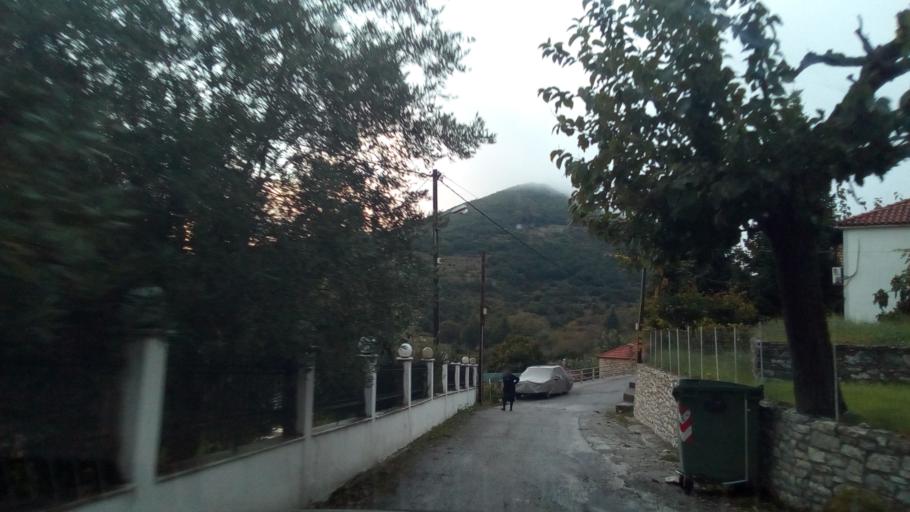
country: GR
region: West Greece
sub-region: Nomos Aitolias kai Akarnanias
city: Nafpaktos
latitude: 38.4844
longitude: 21.7704
